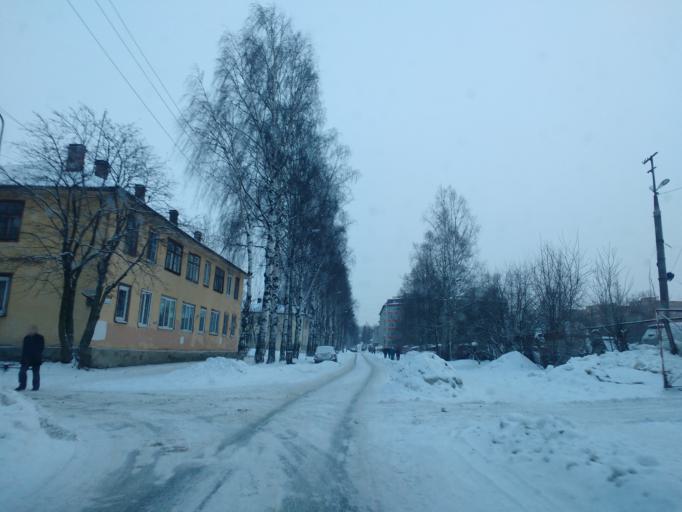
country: RU
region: Republic of Karelia
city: Petrozavodsk
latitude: 61.7806
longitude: 34.3925
